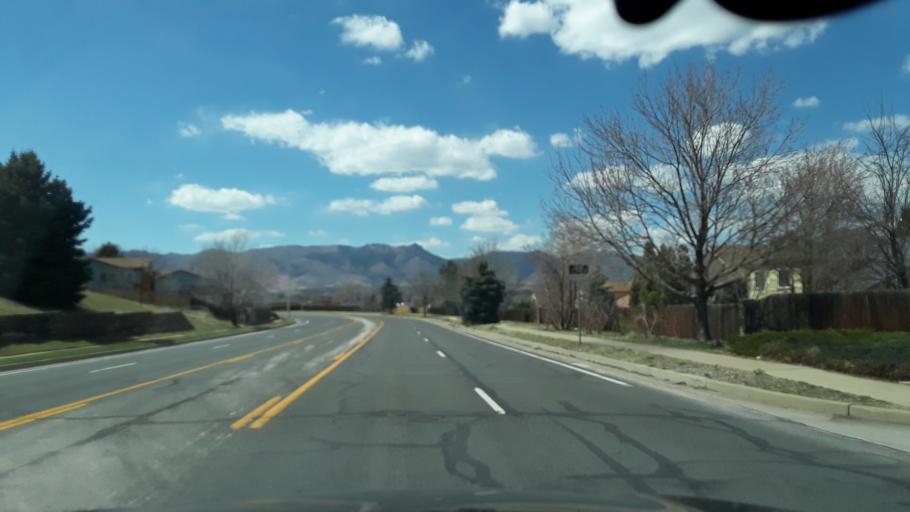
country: US
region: Colorado
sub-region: El Paso County
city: Colorado Springs
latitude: 38.9154
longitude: -104.7807
